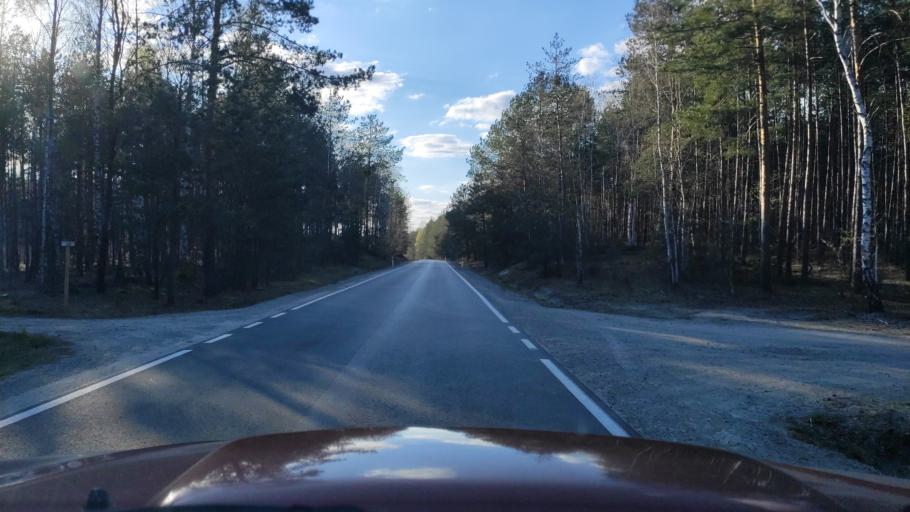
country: PL
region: Masovian Voivodeship
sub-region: Powiat zwolenski
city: Zwolen
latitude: 51.4057
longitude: 21.5290
